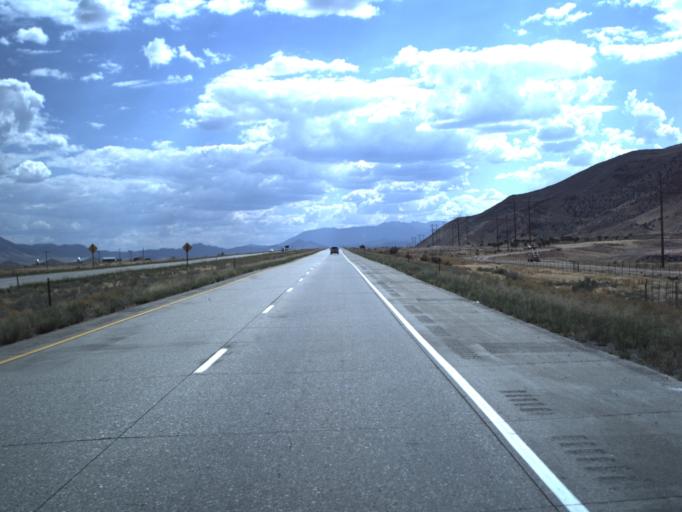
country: US
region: Utah
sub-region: Sevier County
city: Richfield
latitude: 38.7186
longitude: -112.1334
